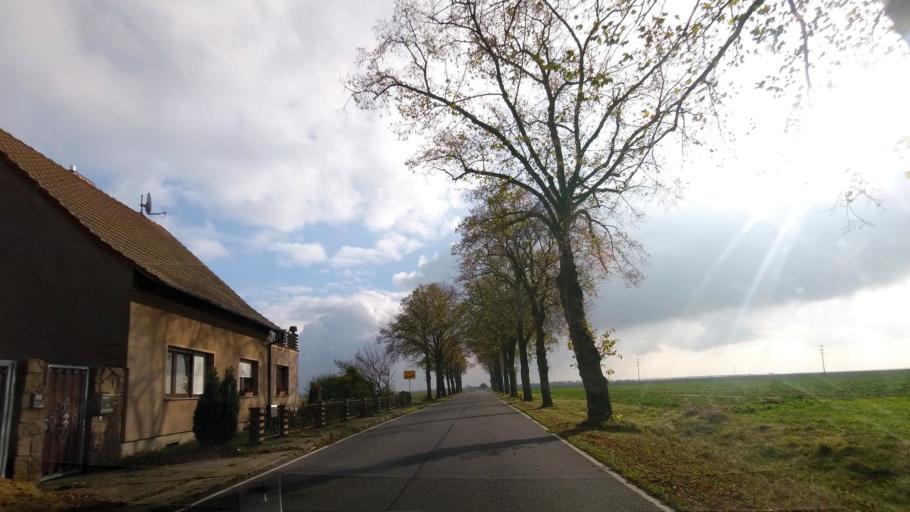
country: DE
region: Brandenburg
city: Niedergorsdorf
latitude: 51.9835
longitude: 12.9483
